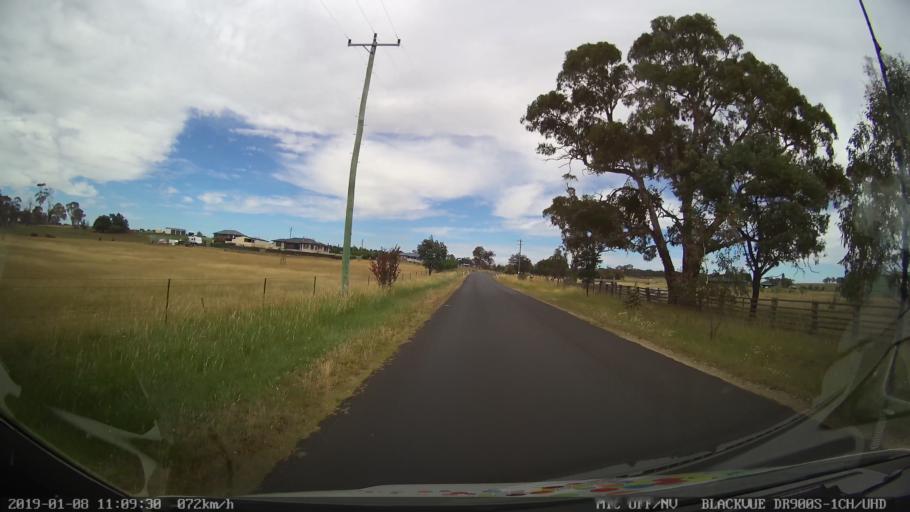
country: AU
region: New South Wales
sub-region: Guyra
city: Guyra
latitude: -30.2258
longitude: 151.6463
